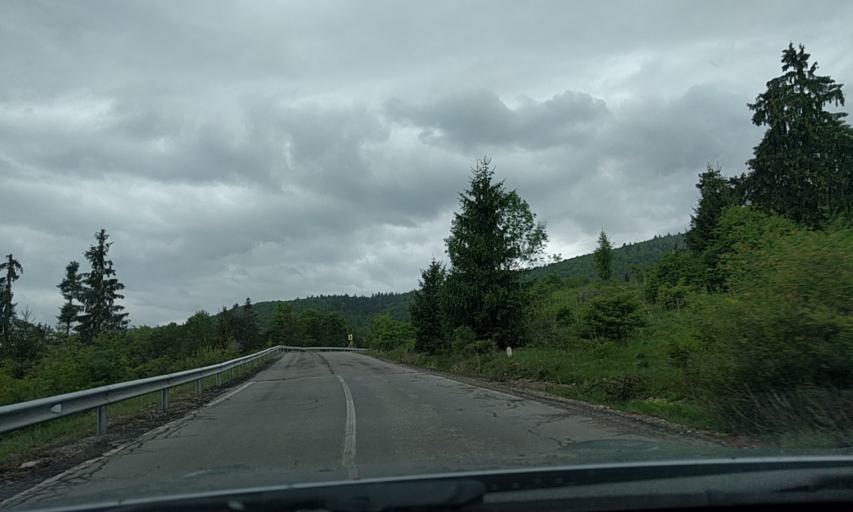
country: RO
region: Prahova
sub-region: Oras Sinaia
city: Sinaia
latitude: 45.3050
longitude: 25.5183
